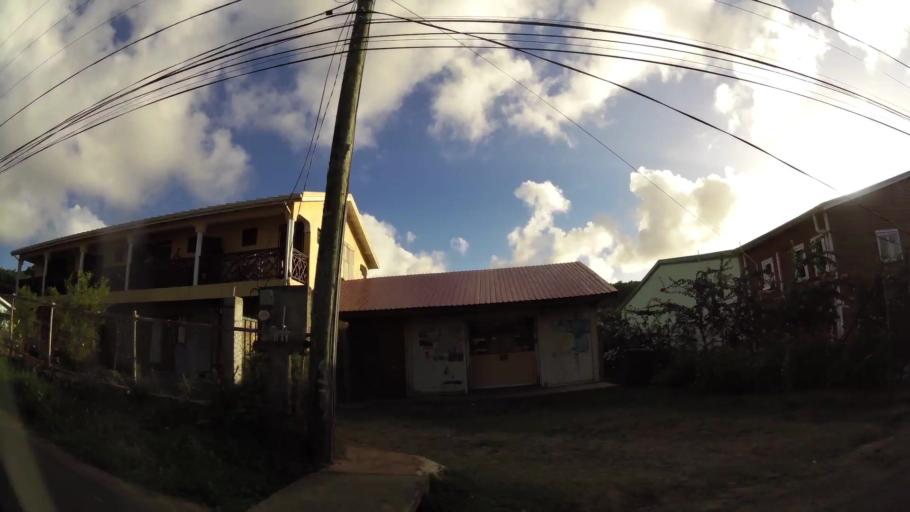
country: LC
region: Gros-Islet
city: Gros Islet
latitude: 14.0772
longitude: -60.9410
